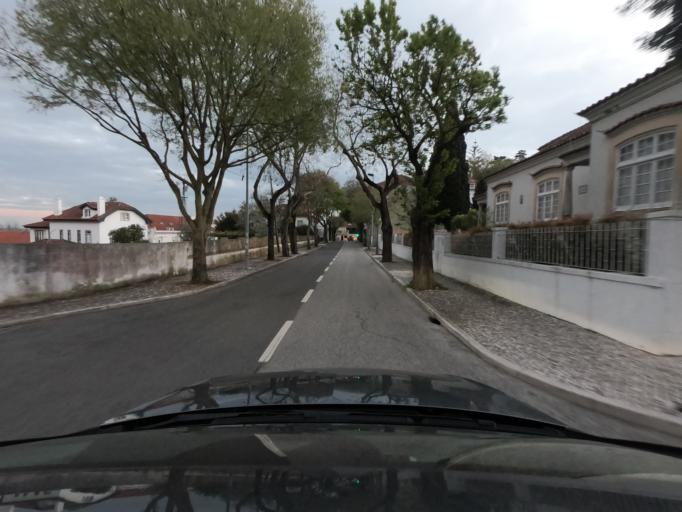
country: PT
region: Lisbon
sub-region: Oeiras
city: Terrugem
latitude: 38.7014
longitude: -9.2779
